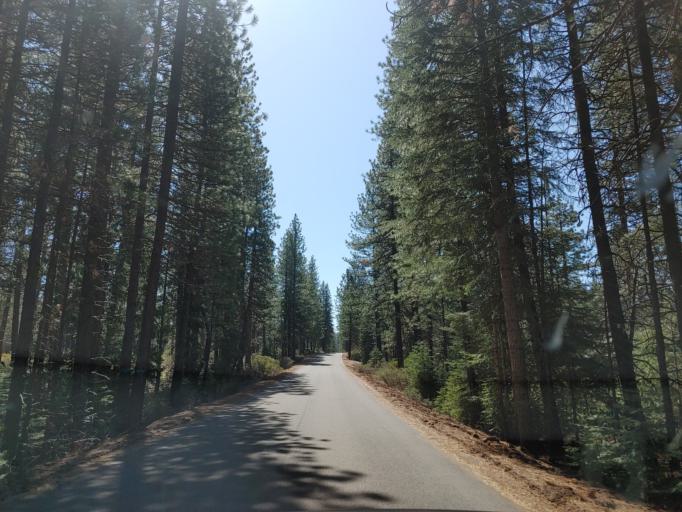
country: US
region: California
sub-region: Siskiyou County
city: McCloud
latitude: 41.2428
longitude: -122.0072
